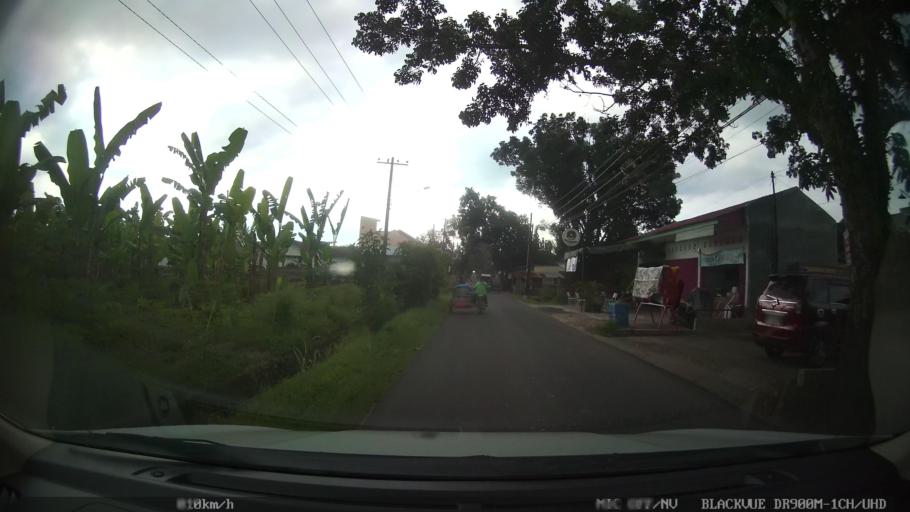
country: ID
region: North Sumatra
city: Sunggal
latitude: 3.5239
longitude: 98.6148
